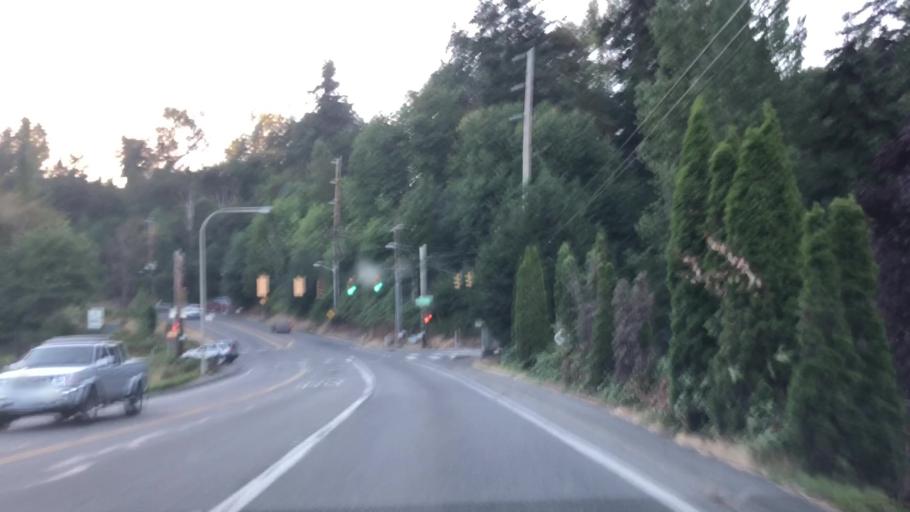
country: US
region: Washington
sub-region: King County
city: Auburn
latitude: 47.3153
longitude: -122.2047
